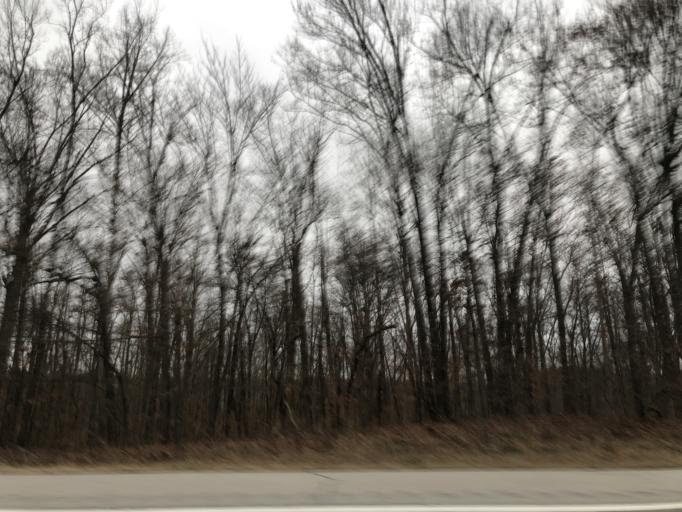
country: US
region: Illinois
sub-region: Johnson County
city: Vienna
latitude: 37.3419
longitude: -88.7866
